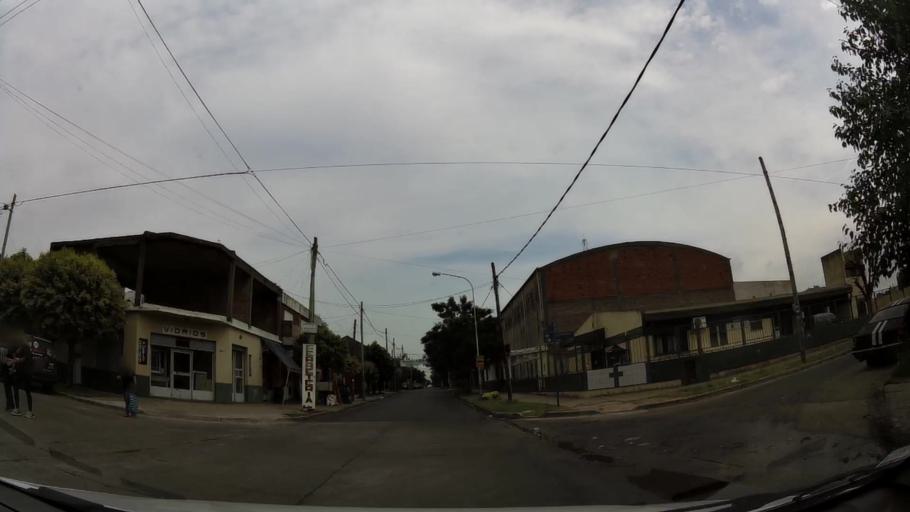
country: AR
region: Buenos Aires
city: San Justo
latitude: -34.6996
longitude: -58.5263
